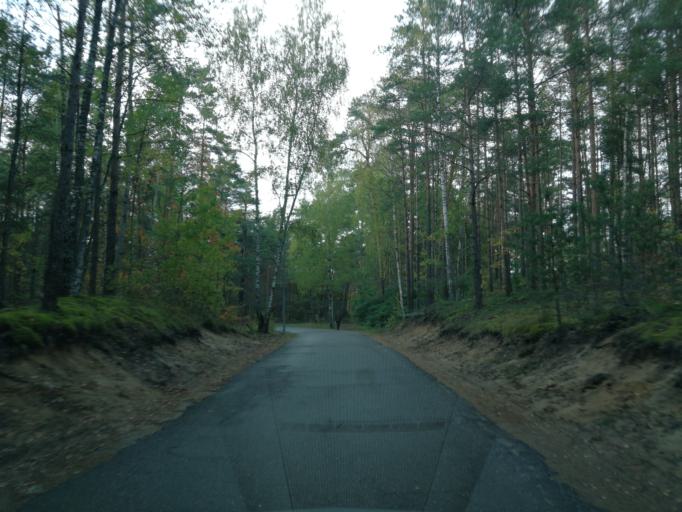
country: LV
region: Riga
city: Jaunciems
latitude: 57.0834
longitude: 24.1561
